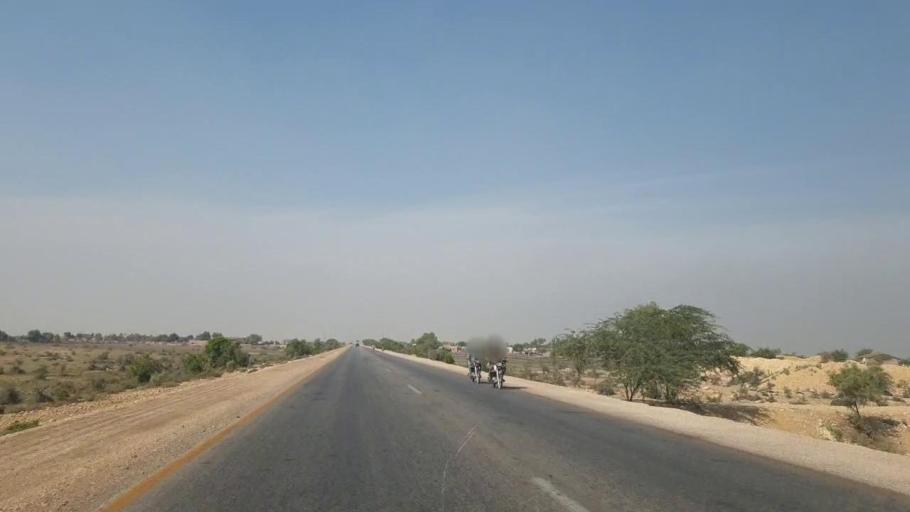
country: PK
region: Sindh
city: Hala
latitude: 25.8730
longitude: 68.2536
